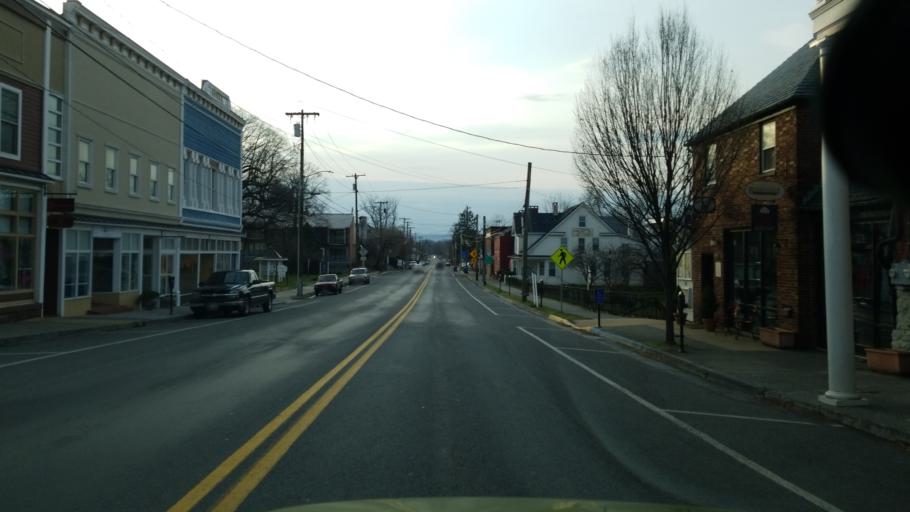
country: US
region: Virginia
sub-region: Clarke County
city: Berryville
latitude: 39.1508
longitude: -77.9809
